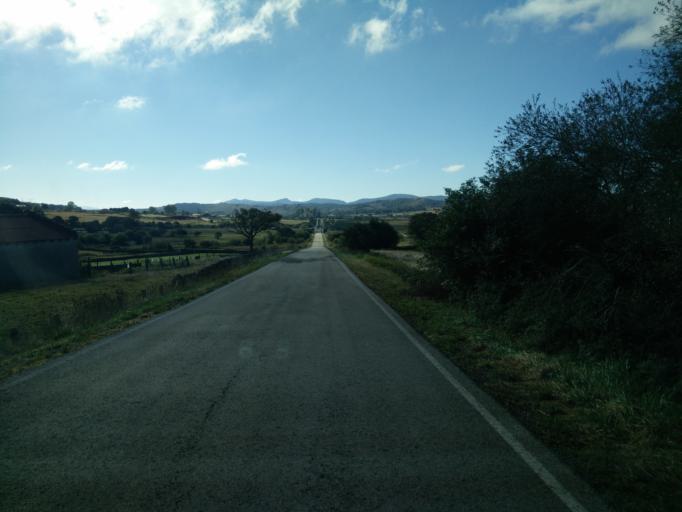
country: ES
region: Castille and Leon
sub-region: Provincia de Burgos
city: Arija
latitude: 43.0275
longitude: -3.8588
